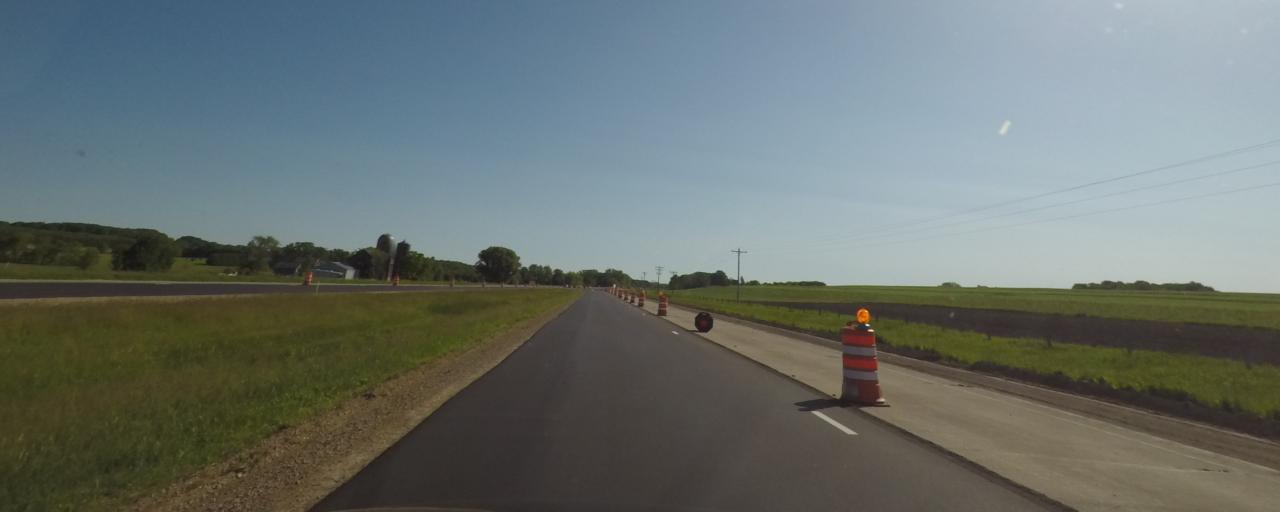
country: US
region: Wisconsin
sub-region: Columbia County
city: Columbus
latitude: 43.3748
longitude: -88.9669
